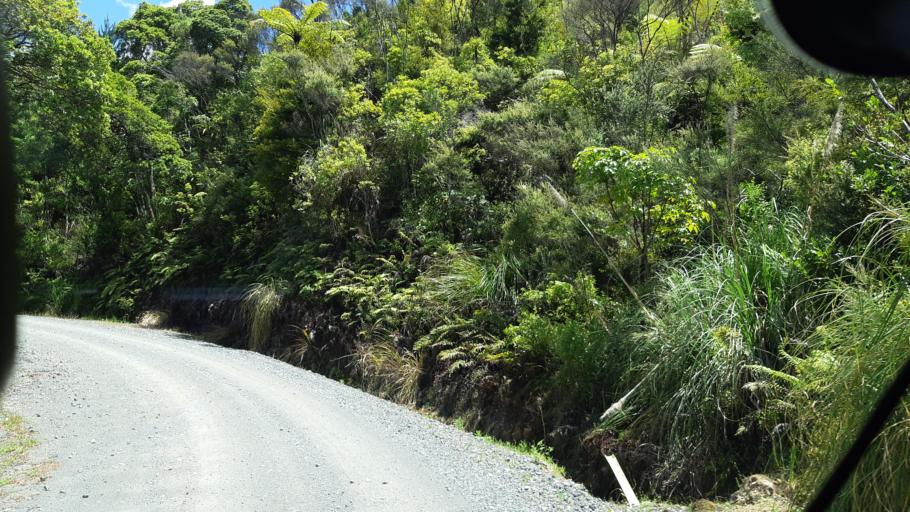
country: NZ
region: Northland
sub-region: Far North District
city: Kaitaia
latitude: -35.2158
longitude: 173.3098
